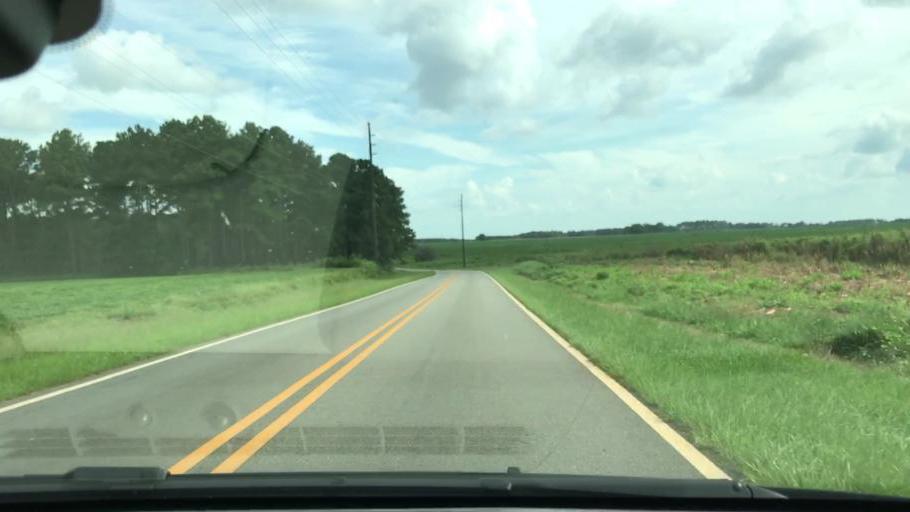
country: US
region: Georgia
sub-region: Clay County
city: Fort Gaines
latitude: 31.5345
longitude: -84.9588
